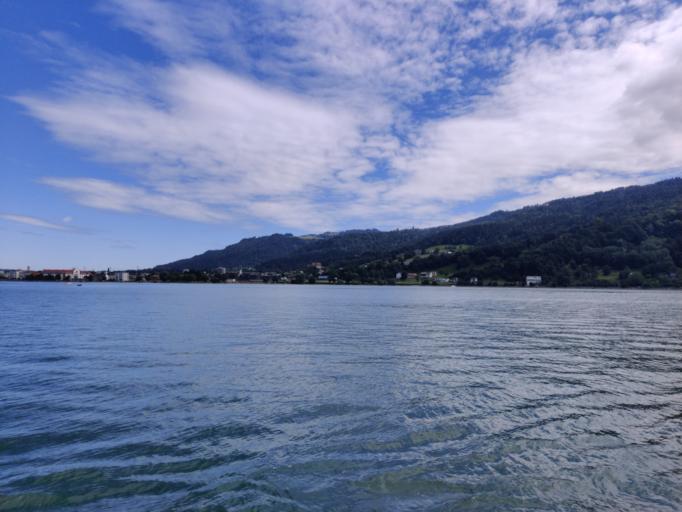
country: AT
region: Vorarlberg
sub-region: Politischer Bezirk Bregenz
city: Bregenz
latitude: 47.5166
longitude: 9.7402
